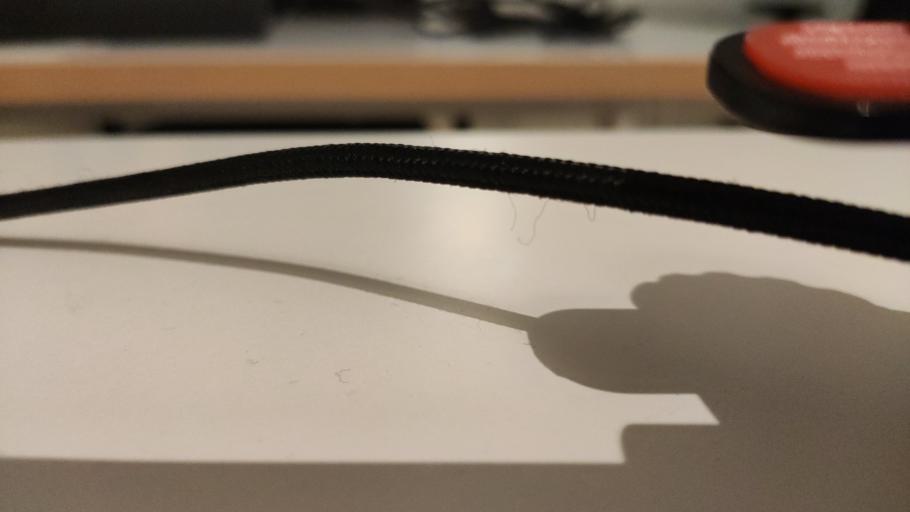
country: RU
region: Moskovskaya
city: Rogachevo
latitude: 56.4110
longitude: 37.2274
